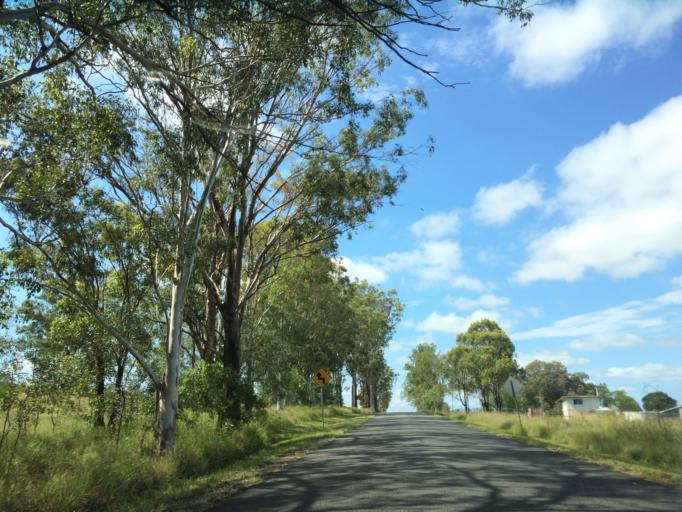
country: AU
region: Queensland
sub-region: Logan
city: Cedar Vale
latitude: -27.8847
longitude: 152.9722
